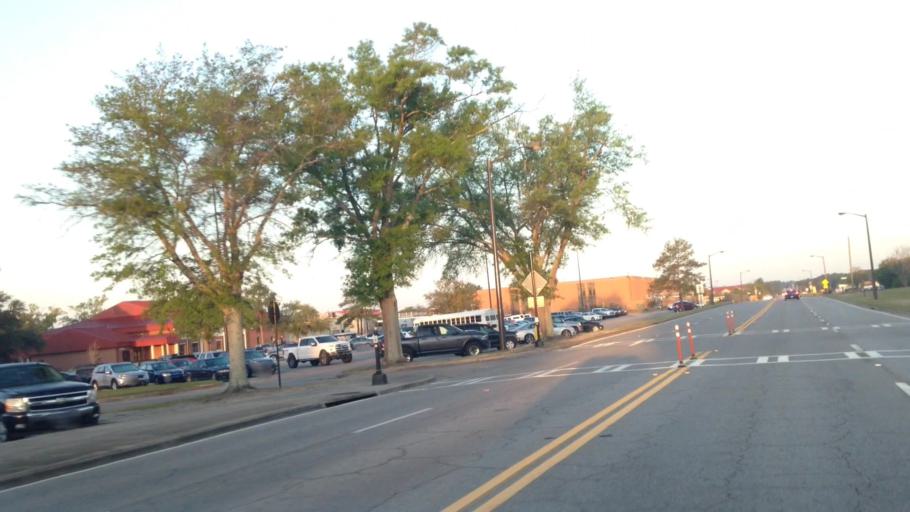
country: US
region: Georgia
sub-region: Columbia County
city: Grovetown
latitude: 33.4254
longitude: -82.1502
